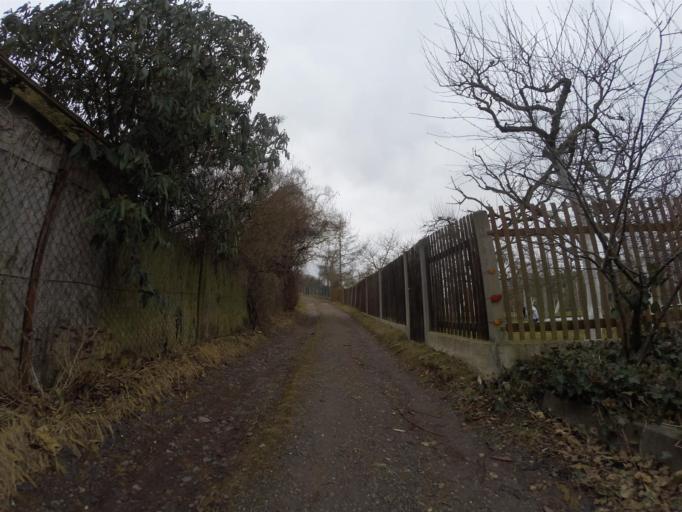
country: DE
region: Thuringia
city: Jena
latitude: 50.9148
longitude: 11.5695
